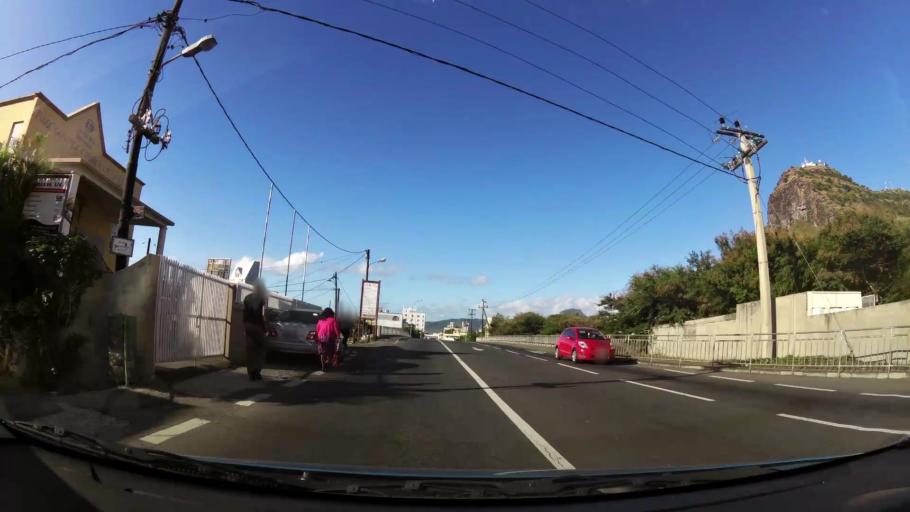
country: MU
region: Port Louis
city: Port Louis
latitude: -20.1684
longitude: 57.4844
